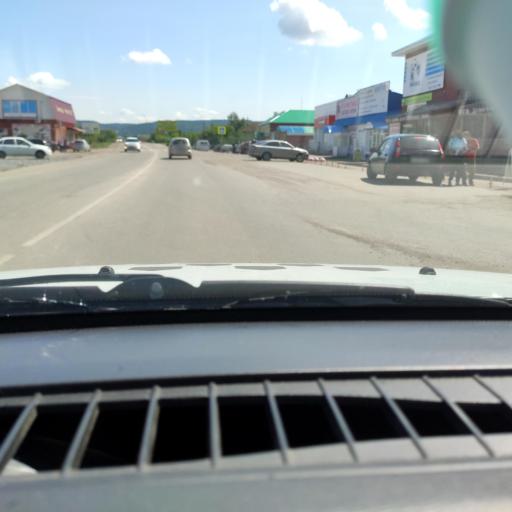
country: RU
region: Bashkortostan
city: Mesyagutovo
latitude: 55.5324
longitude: 58.2494
